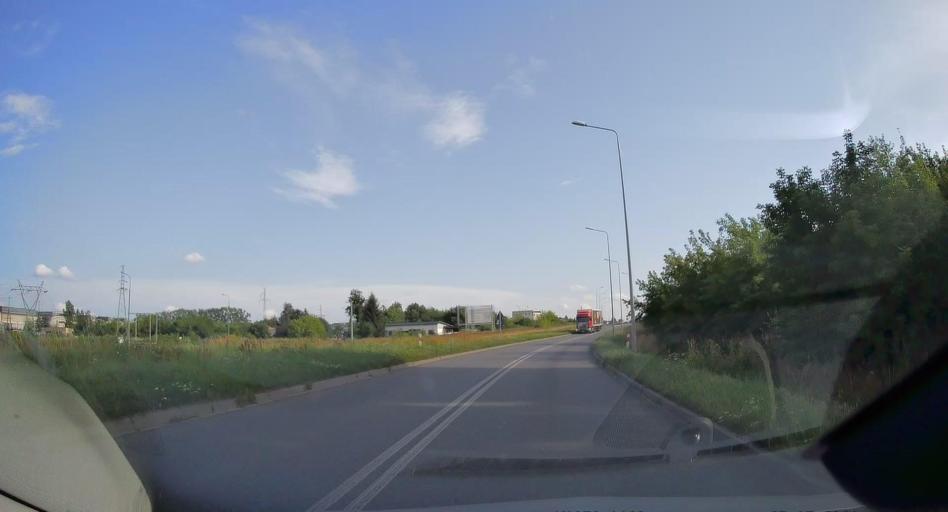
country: PL
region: Swietokrzyskie
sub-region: Powiat konecki
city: Konskie
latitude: 51.2033
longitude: 20.4003
